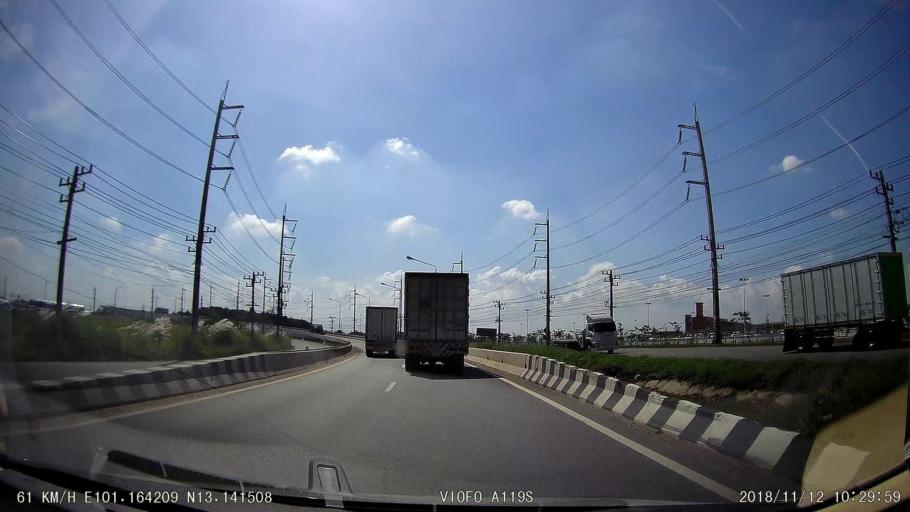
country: TH
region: Rayong
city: Pluak Daeng
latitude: 13.1327
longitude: 101.1663
